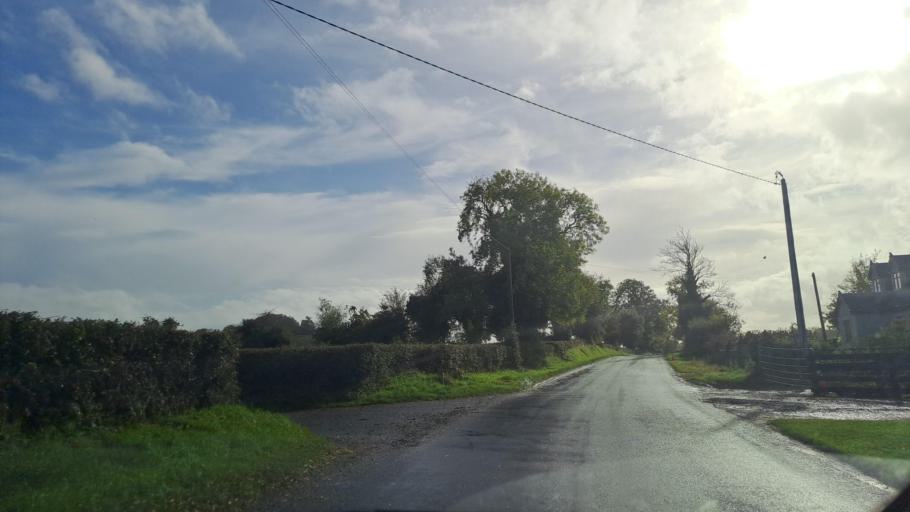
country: IE
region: Leinster
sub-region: Lu
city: Ardee
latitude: 53.8586
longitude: -6.6573
